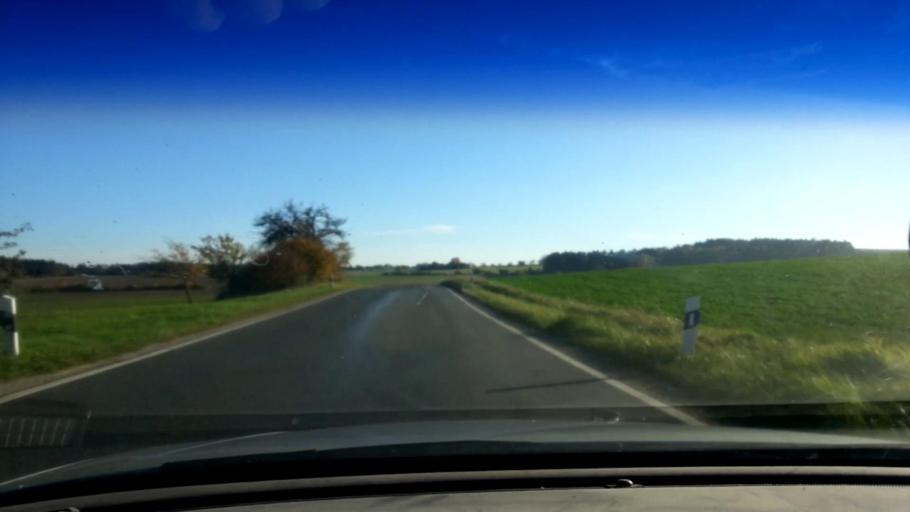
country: DE
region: Bavaria
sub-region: Upper Franconia
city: Poxdorf
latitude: 49.9030
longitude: 11.0922
